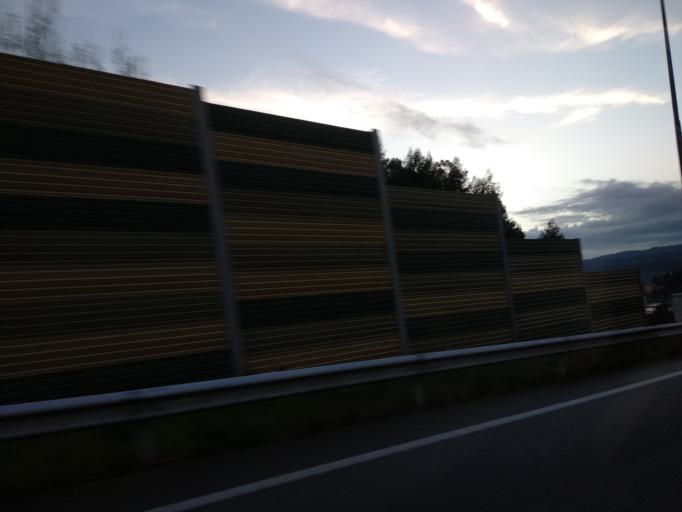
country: PT
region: Braga
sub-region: Braga
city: Oliveira
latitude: 41.4950
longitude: -8.4663
